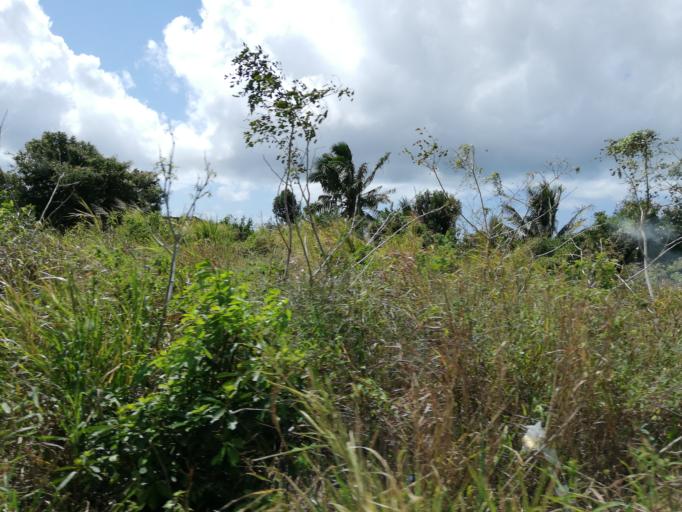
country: MU
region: Riviere du Rempart
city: Esperance Trebuchet
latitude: -20.0734
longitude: 57.6444
